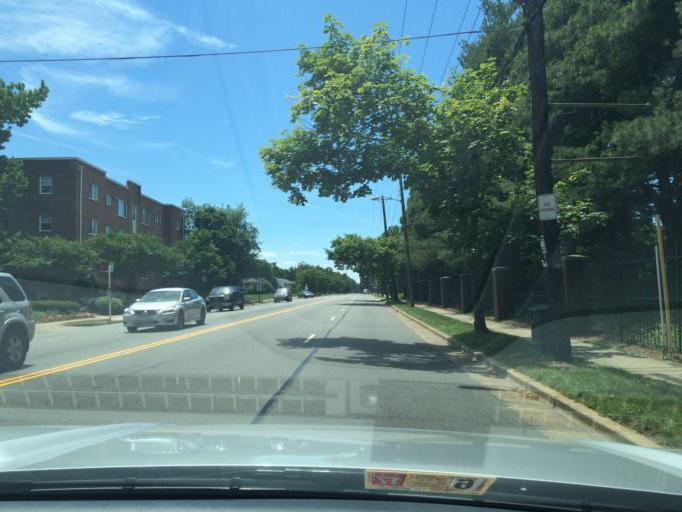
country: US
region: Virginia
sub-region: Fairfax County
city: Huntington
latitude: 38.8260
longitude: -77.0886
